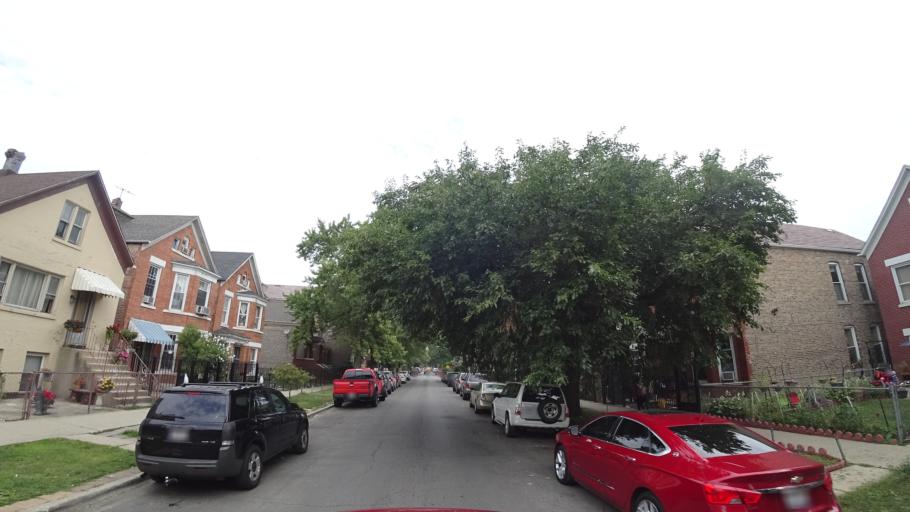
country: US
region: Illinois
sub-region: Cook County
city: Cicero
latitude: 41.8418
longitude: -87.7123
